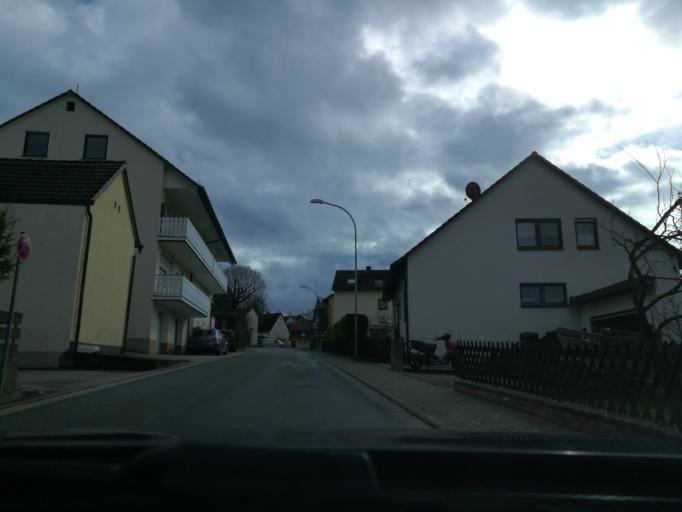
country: DE
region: Bavaria
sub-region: Regierungsbezirk Mittelfranken
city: Rottenbach
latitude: 49.6692
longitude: 10.9307
